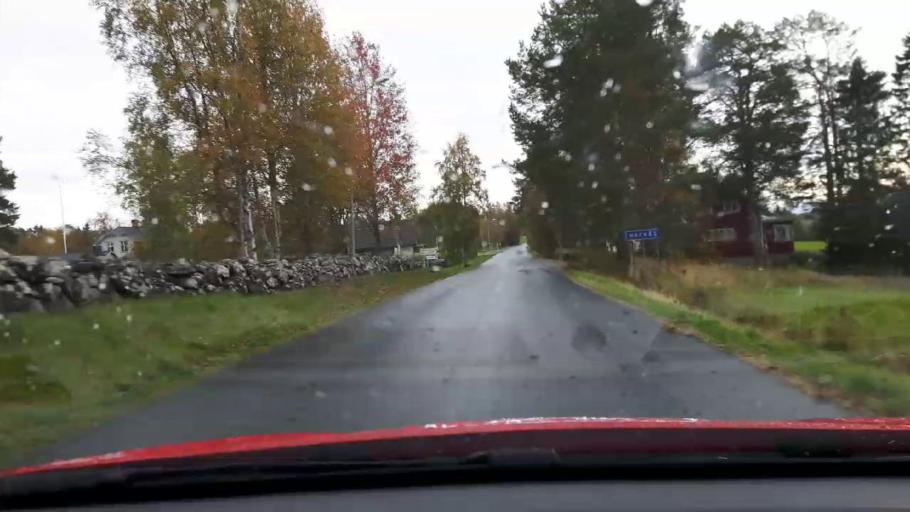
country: SE
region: Jaemtland
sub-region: Bergs Kommun
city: Hoverberg
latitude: 62.9346
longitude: 14.5142
